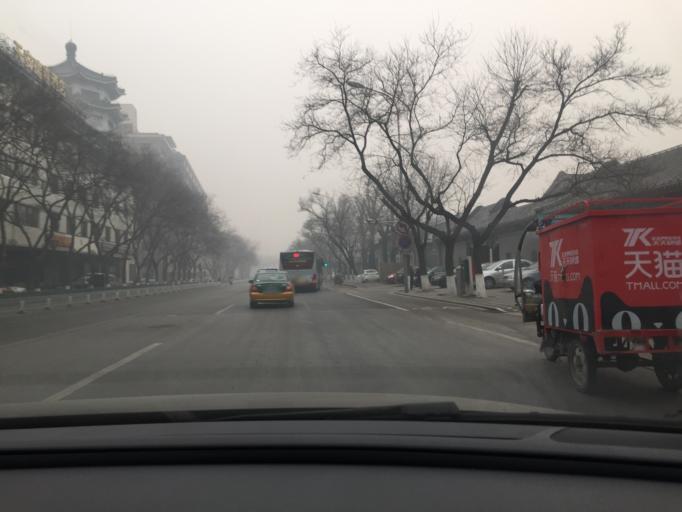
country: CN
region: Beijing
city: Beijing
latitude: 39.9093
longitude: 116.4005
